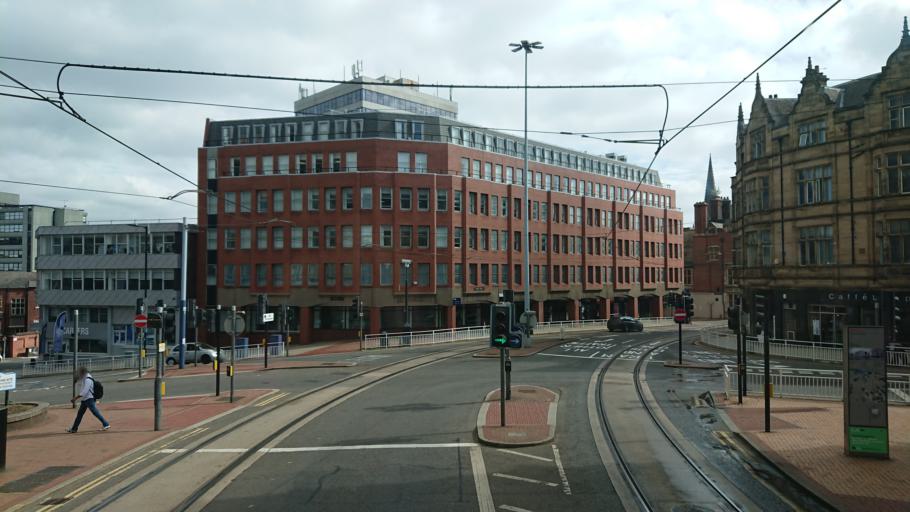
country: GB
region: England
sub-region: Sheffield
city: Sheffield
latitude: 53.3822
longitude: -1.4720
